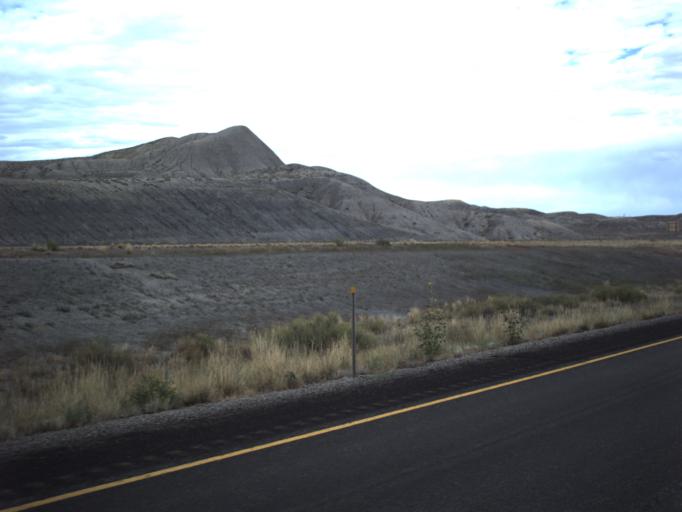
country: US
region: Utah
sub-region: Grand County
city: Moab
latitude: 38.9540
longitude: -109.7034
